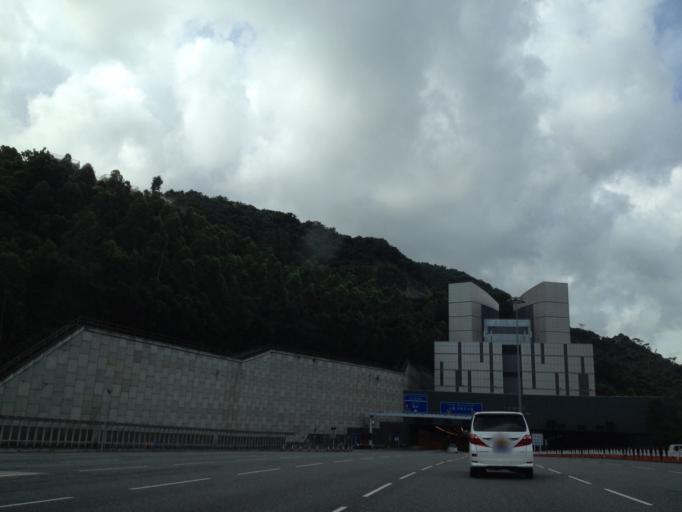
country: HK
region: Wong Tai Sin
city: Wong Tai Sin
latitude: 22.3596
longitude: 114.1631
